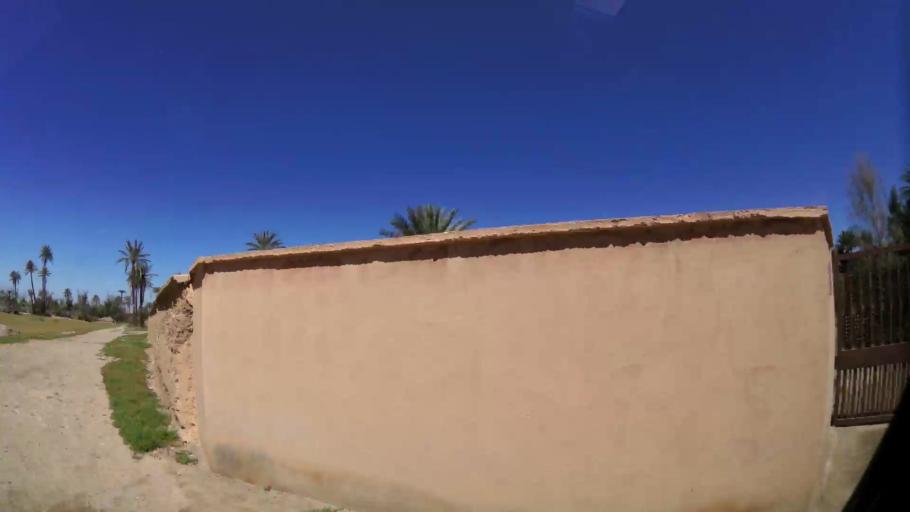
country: MA
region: Marrakech-Tensift-Al Haouz
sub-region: Marrakech
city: Marrakesh
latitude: 31.6786
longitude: -7.9790
